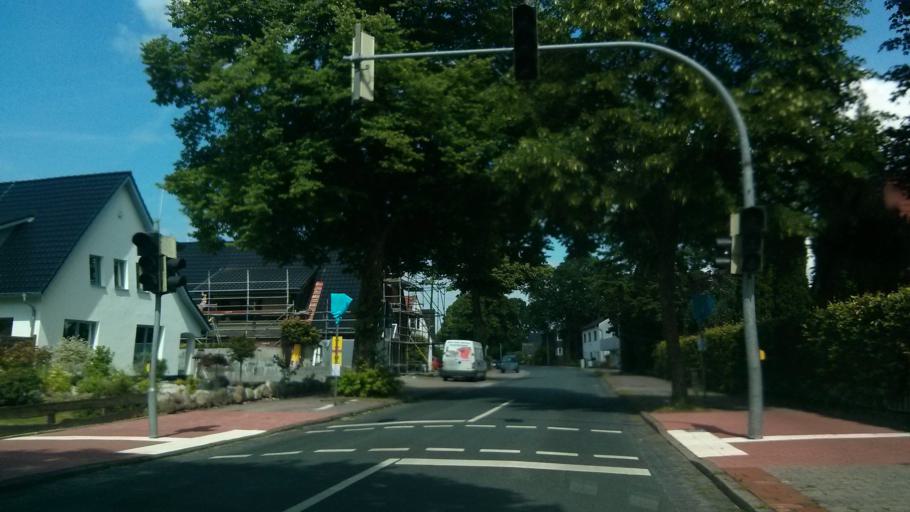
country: DE
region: Lower Saxony
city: Loxstedt
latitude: 53.4841
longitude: 8.6845
